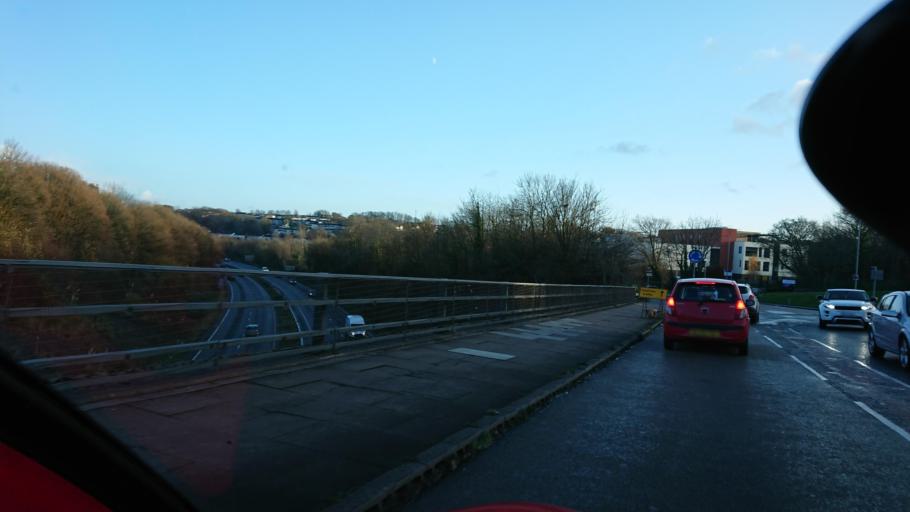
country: GB
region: England
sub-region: Plymouth
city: Plymouth
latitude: 50.4044
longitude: -4.1573
